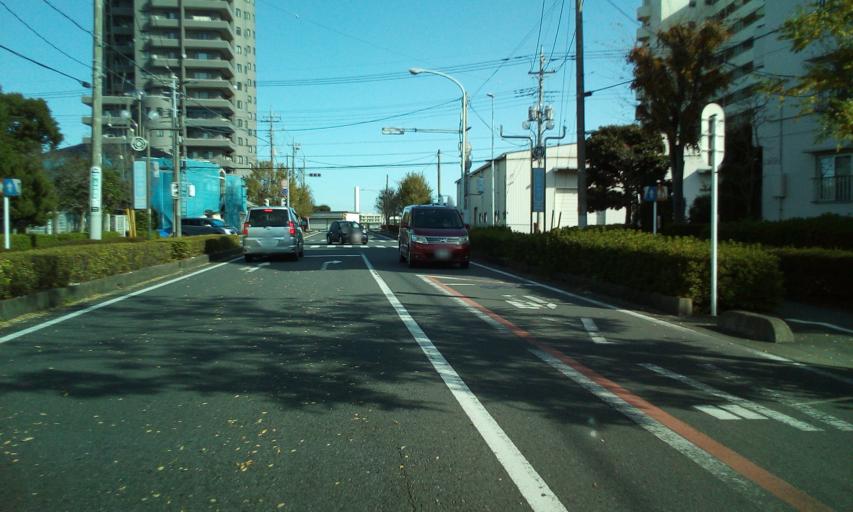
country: JP
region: Chiba
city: Nagareyama
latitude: 35.8588
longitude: 139.8883
